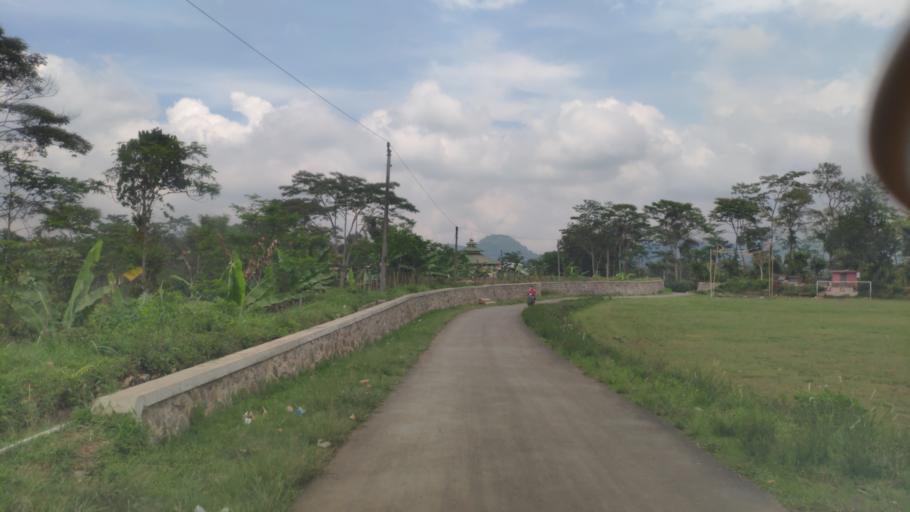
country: ID
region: Central Java
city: Wonosobo
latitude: -7.2655
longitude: 109.7964
